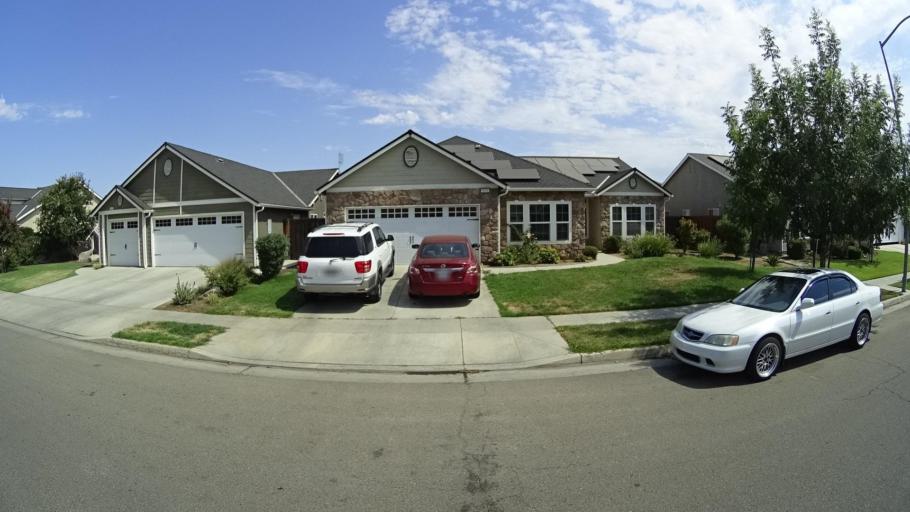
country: US
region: California
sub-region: Fresno County
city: Tarpey Village
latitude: 36.7806
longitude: -119.6667
